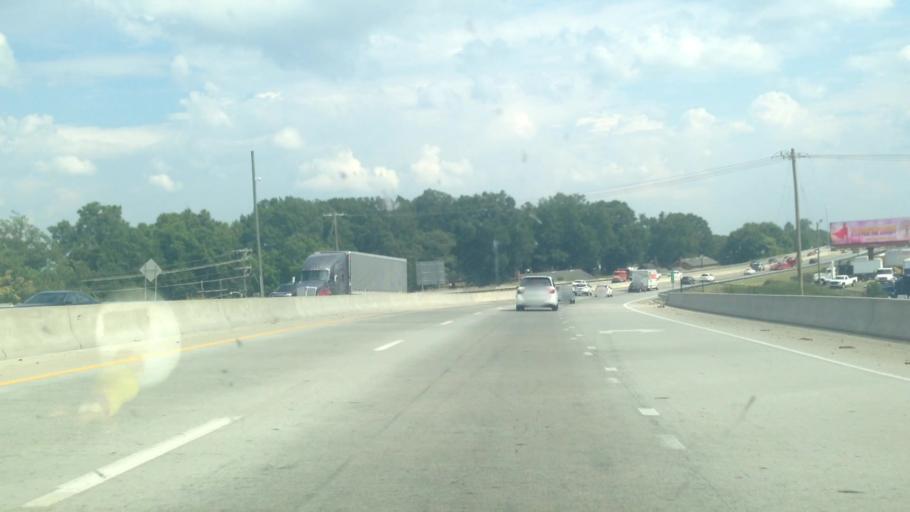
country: US
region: North Carolina
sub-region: Forsyth County
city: Winston-Salem
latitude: 36.1273
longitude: -80.2335
